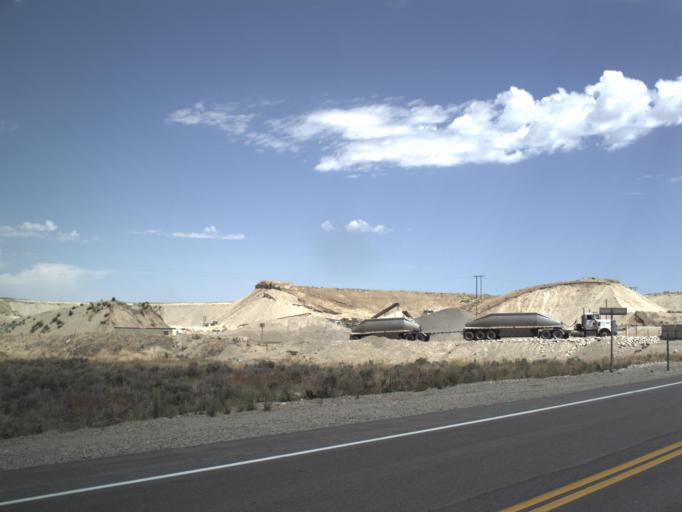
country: US
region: Utah
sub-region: Tooele County
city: Tooele
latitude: 40.4587
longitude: -112.3579
